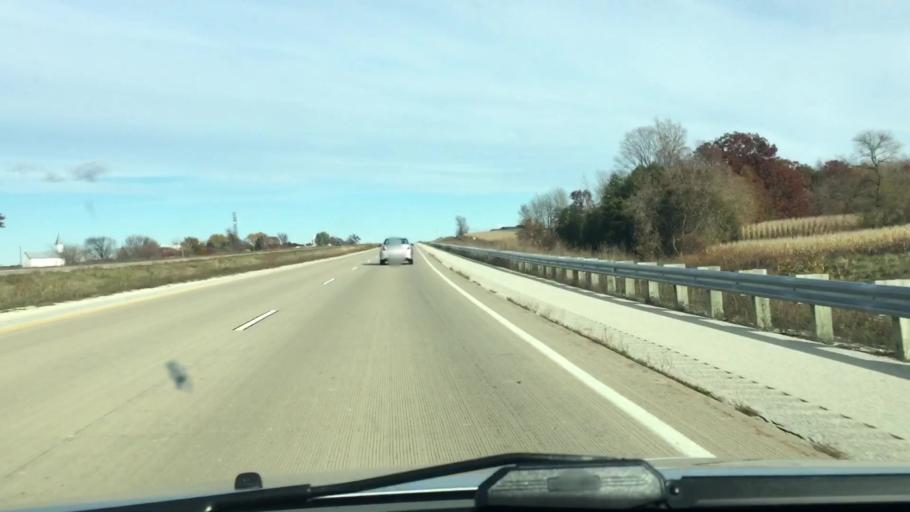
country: US
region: Wisconsin
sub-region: Kewaunee County
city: Luxemburg
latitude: 44.7077
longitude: -87.7003
